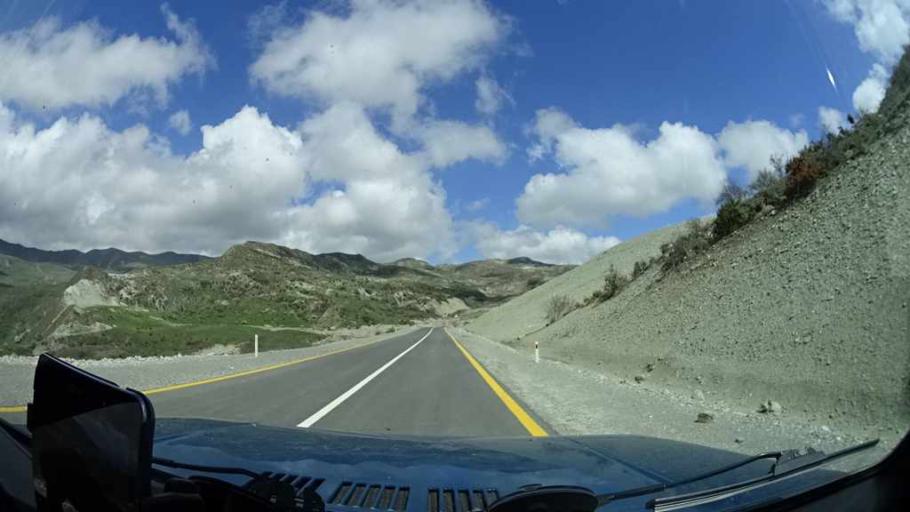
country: AZ
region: Ismayilli
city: Basqal
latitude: 40.8685
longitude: 48.4573
